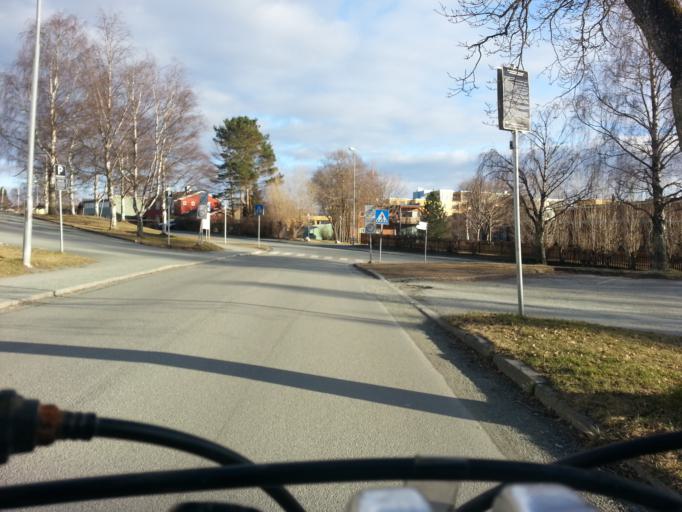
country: NO
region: Sor-Trondelag
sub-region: Trondheim
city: Trondheim
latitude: 63.4500
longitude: 10.4433
